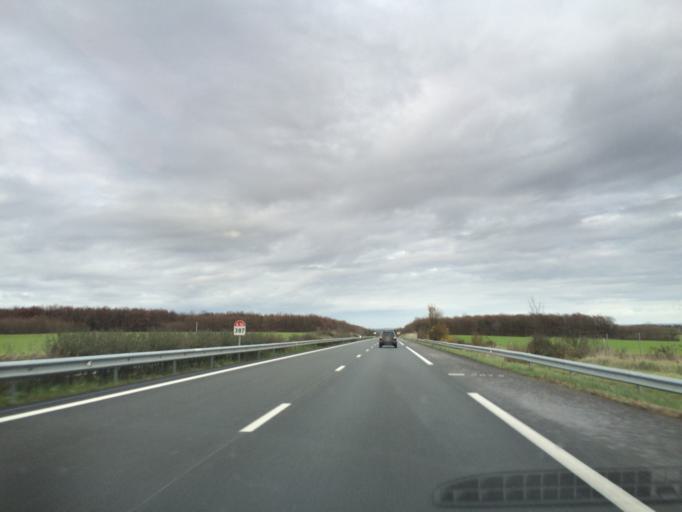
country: FR
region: Poitou-Charentes
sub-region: Departement des Deux-Sevres
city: Beauvoir-sur-Niort
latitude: 46.1874
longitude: -0.4929
